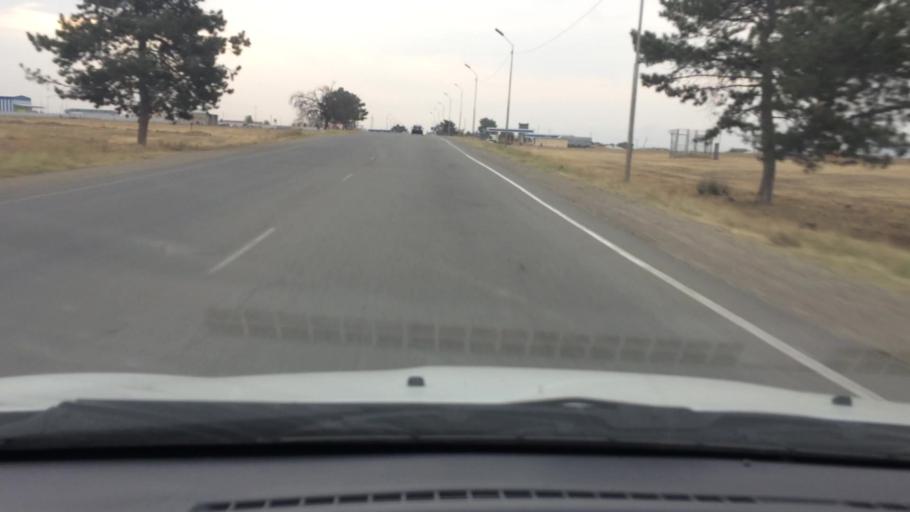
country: GE
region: Kvemo Kartli
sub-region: Marneuli
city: Marneuli
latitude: 41.5125
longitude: 44.7899
